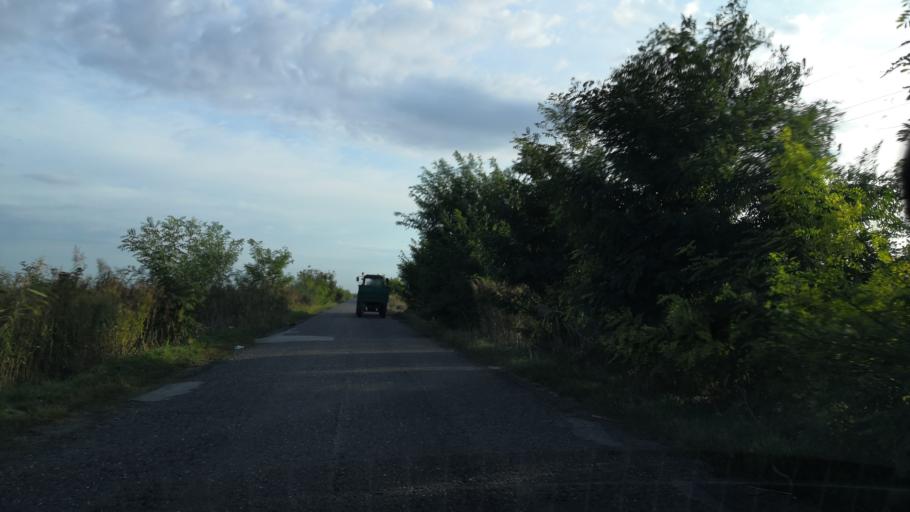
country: RS
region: Autonomna Pokrajina Vojvodina
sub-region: Sremski Okrug
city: Stara Pazova
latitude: 45.0113
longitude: 20.1676
